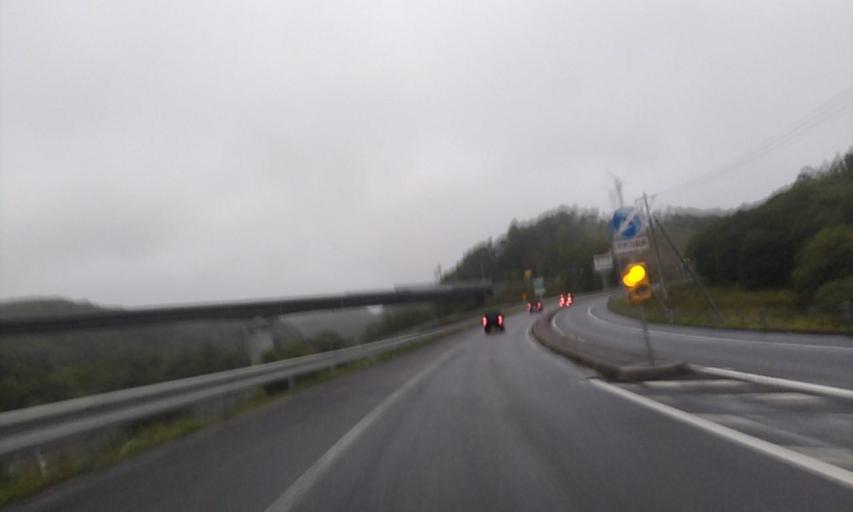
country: JP
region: Hokkaido
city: Kushiro
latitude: 43.0021
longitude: 144.5013
